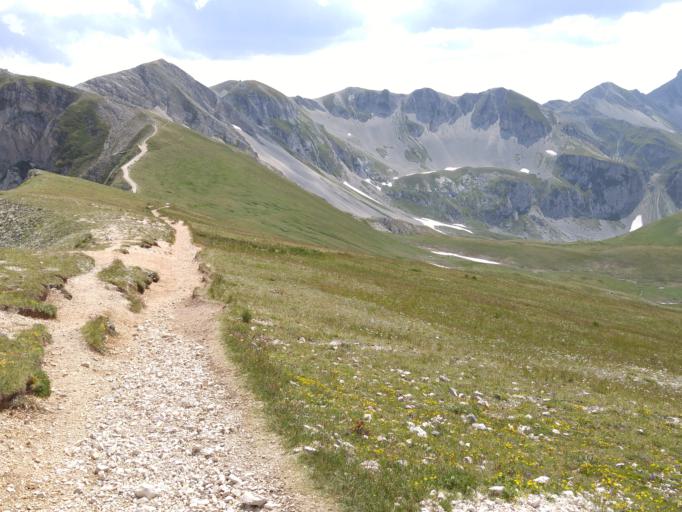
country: IT
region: Abruzzo
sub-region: Provincia di Teramo
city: Pietracamela
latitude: 42.4577
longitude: 13.5612
